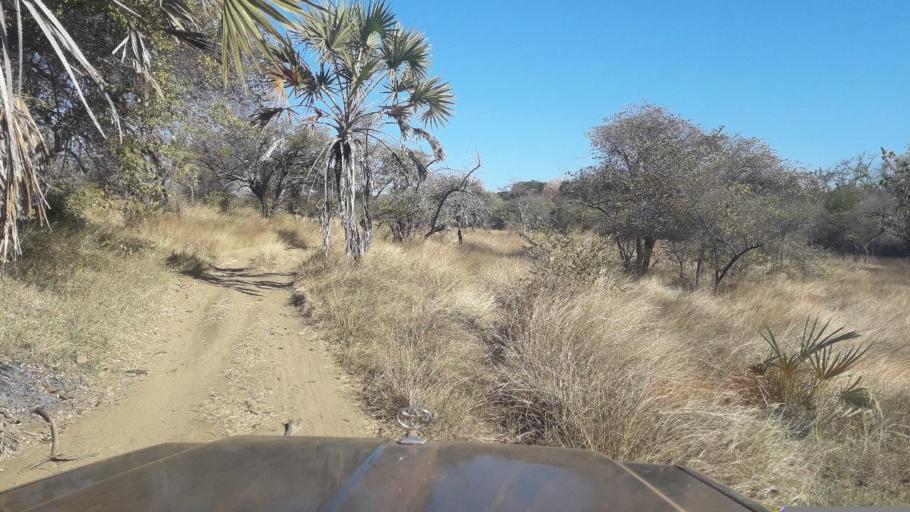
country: MG
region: Boeny
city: Sitampiky
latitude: -16.3926
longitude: 45.5930
